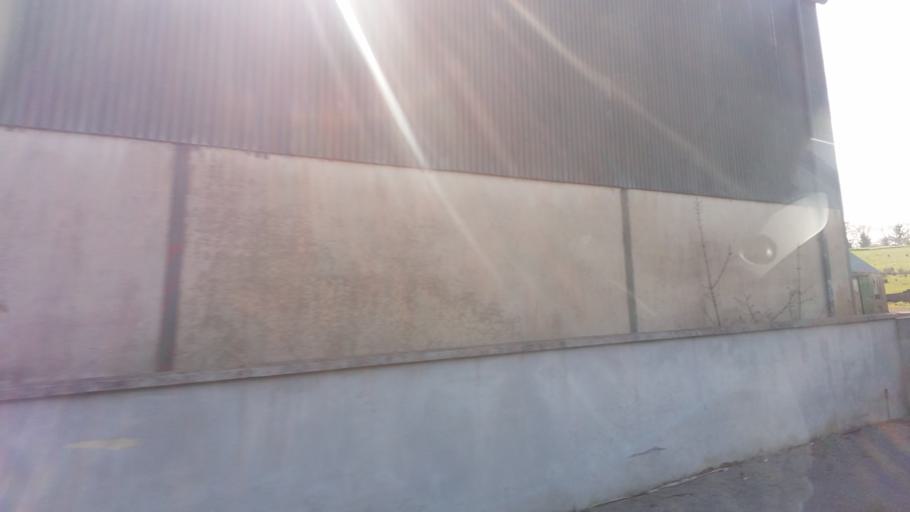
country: GB
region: Northern Ireland
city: Irvinestown
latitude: 54.4483
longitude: -7.7970
